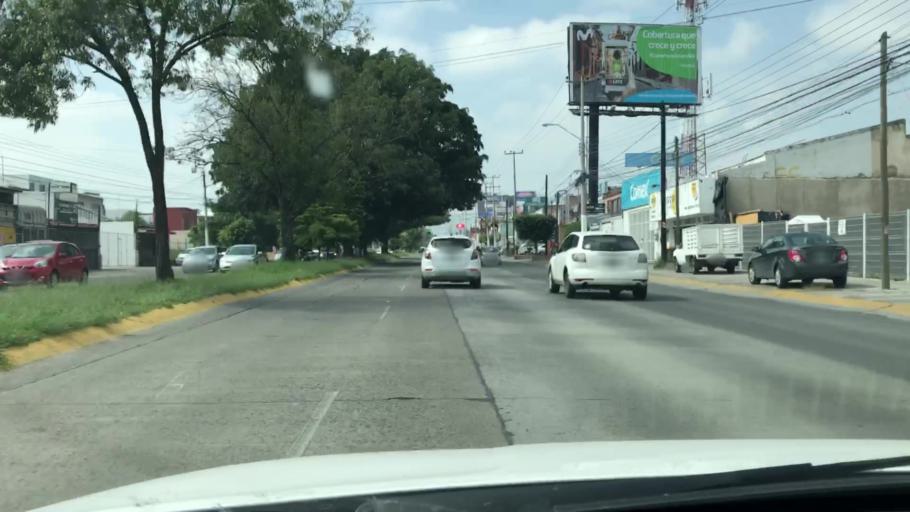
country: MX
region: Jalisco
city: Guadalajara
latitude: 20.6364
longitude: -103.4224
